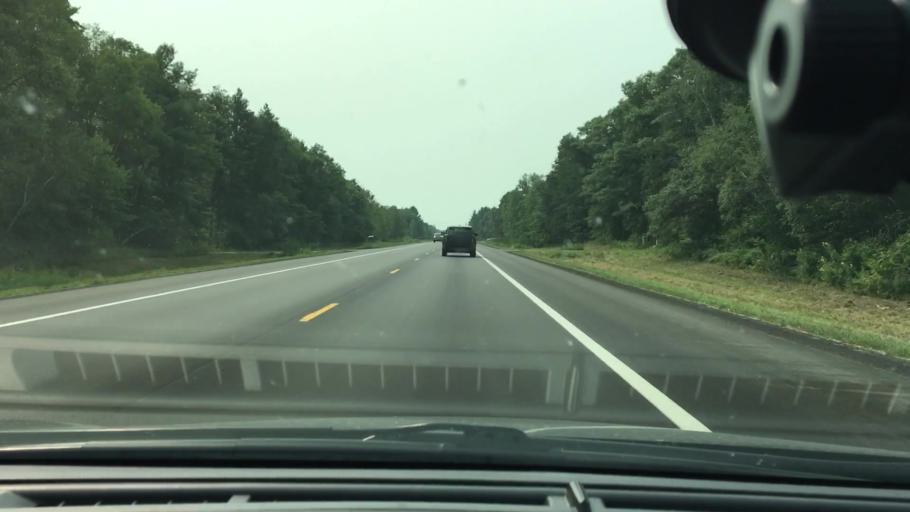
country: US
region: Minnesota
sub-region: Crow Wing County
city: Brainerd
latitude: 46.4540
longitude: -94.1722
